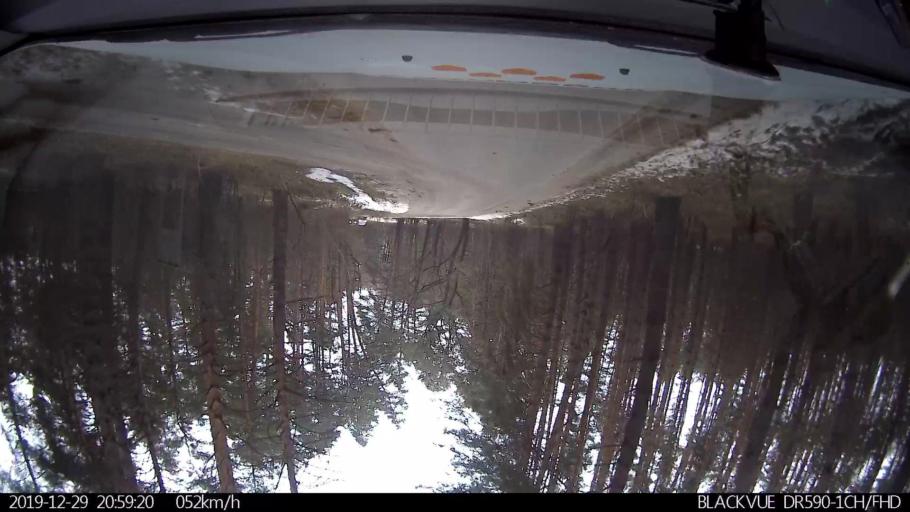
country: RU
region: Nizjnij Novgorod
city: Afonino
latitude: 56.1747
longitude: 43.9905
